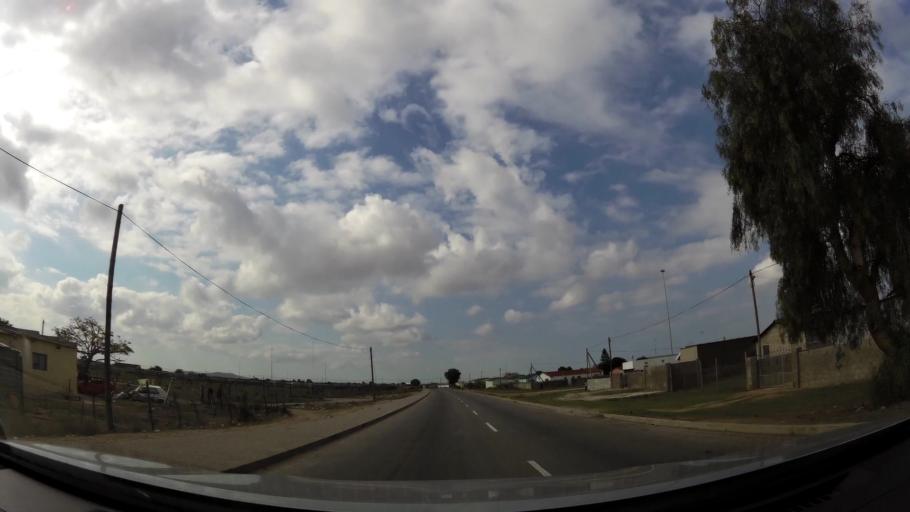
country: ZA
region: Eastern Cape
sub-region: Nelson Mandela Bay Metropolitan Municipality
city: Port Elizabeth
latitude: -33.8073
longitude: 25.5871
